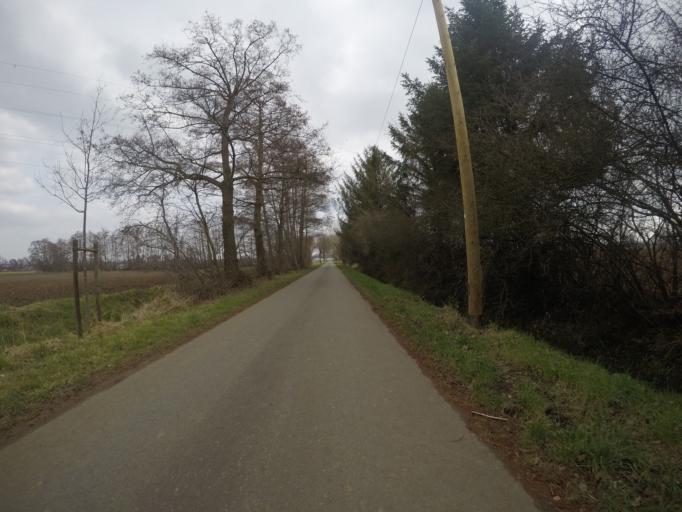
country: DE
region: North Rhine-Westphalia
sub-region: Regierungsbezirk Dusseldorf
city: Hamminkeln
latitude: 51.7748
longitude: 6.5947
